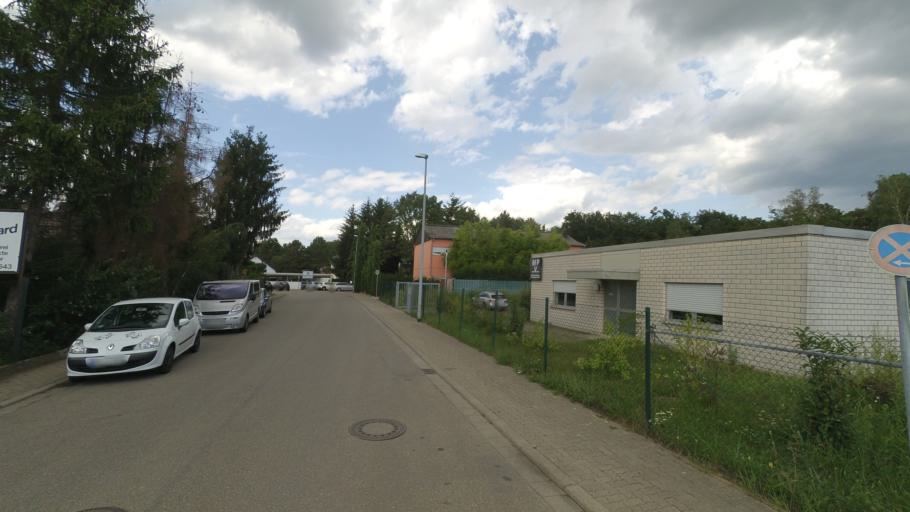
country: DE
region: Rheinland-Pfalz
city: Schifferstadt
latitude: 49.3832
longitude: 8.3973
